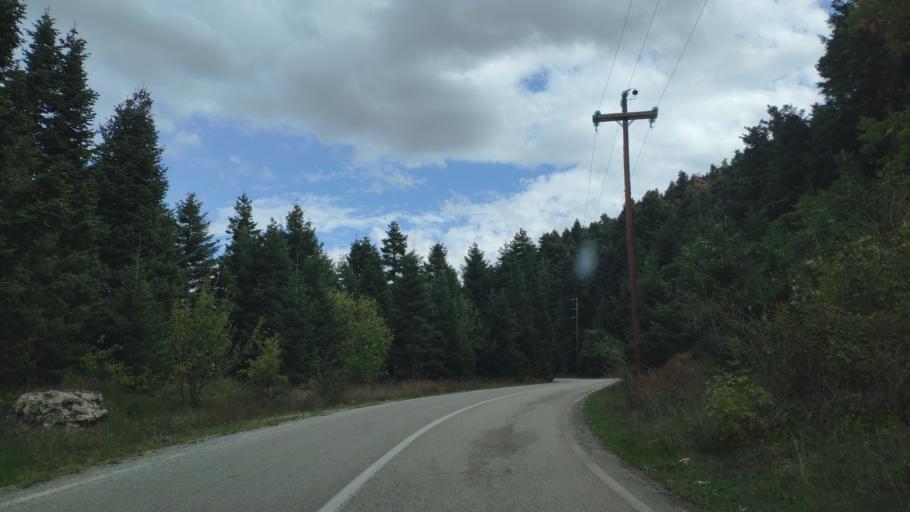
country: GR
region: Central Greece
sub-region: Nomos Fthiotidos
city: Stavros
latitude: 38.7304
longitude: 22.3483
